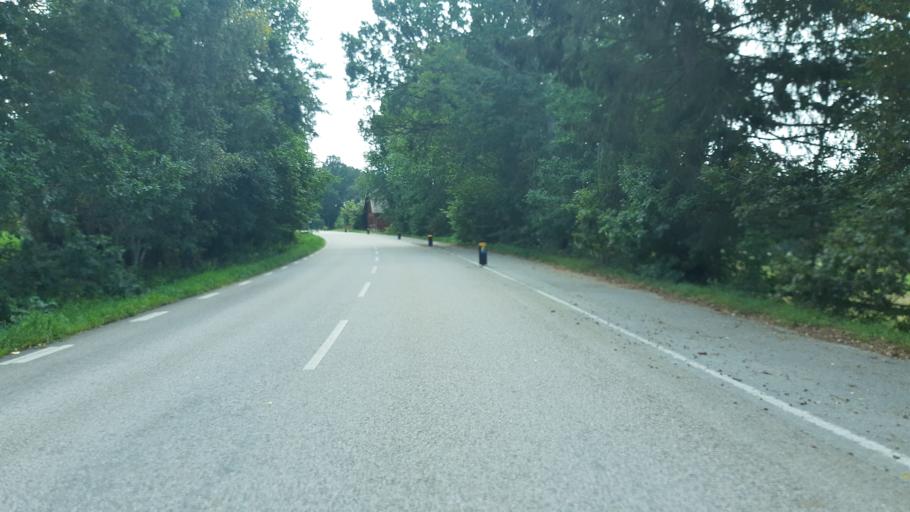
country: SE
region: Blekinge
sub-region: Karlskrona Kommun
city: Nattraby
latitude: 56.2236
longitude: 15.4136
